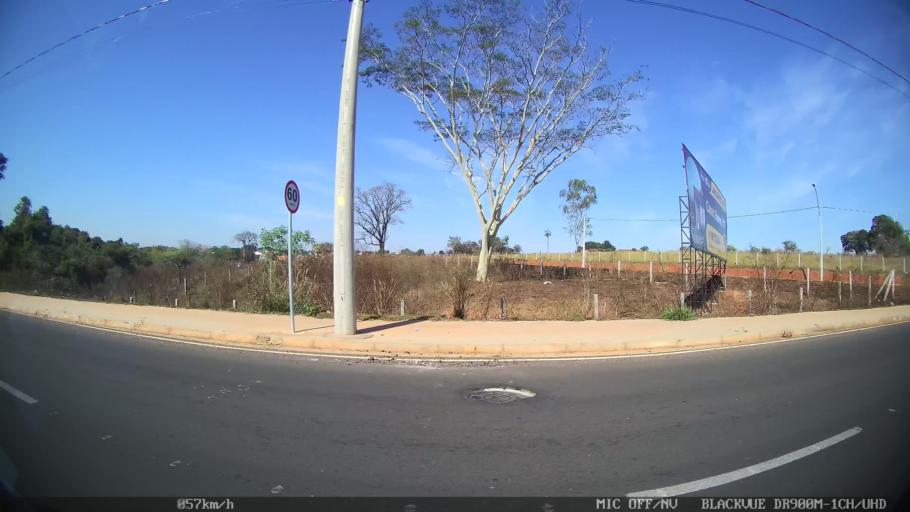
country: BR
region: Sao Paulo
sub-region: Sao Jose Do Rio Preto
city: Sao Jose do Rio Preto
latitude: -20.7628
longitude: -49.3680
